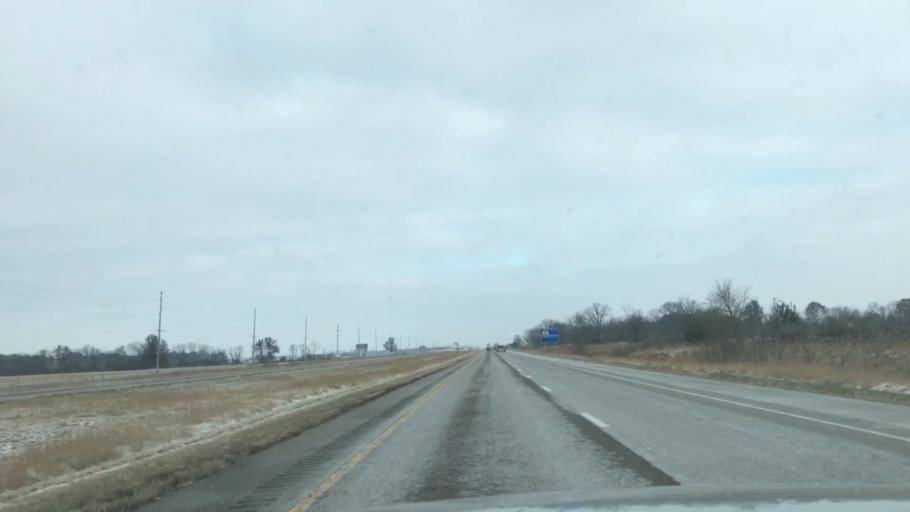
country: US
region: Illinois
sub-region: Macoupin County
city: Staunton
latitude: 38.9864
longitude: -89.7495
